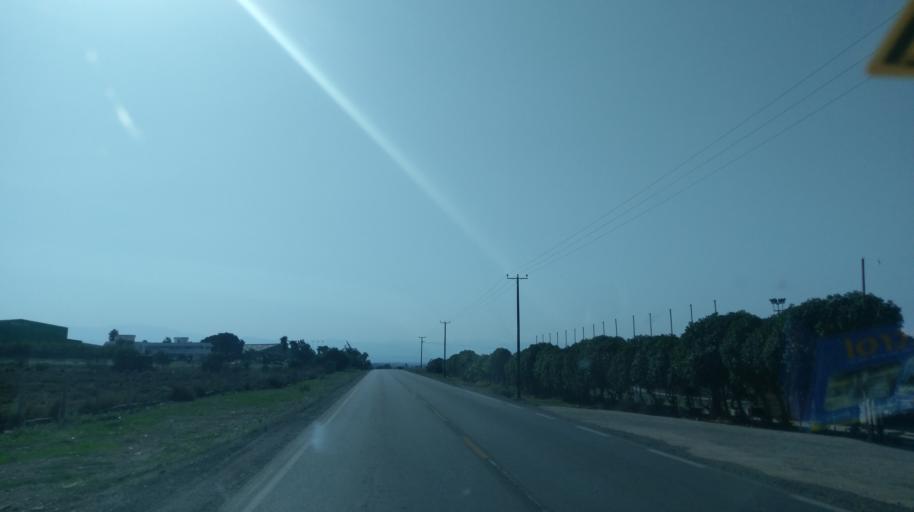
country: CY
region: Lefkosia
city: Morfou
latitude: 35.2320
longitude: 33.0169
